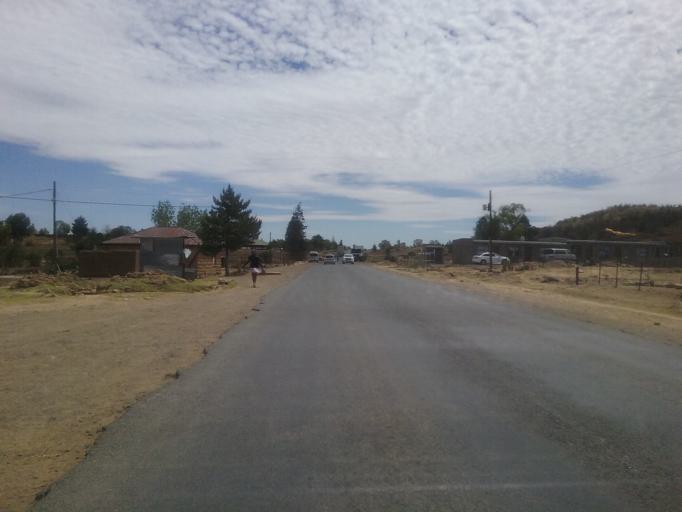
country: LS
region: Mafeteng
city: Mafeteng
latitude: -29.8362
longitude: 27.2328
